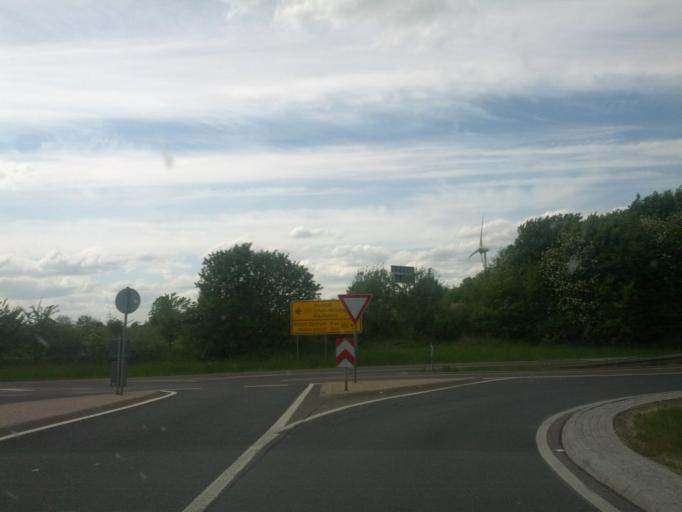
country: DE
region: Thuringia
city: Kirchheim
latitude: 50.9046
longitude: 11.0079
